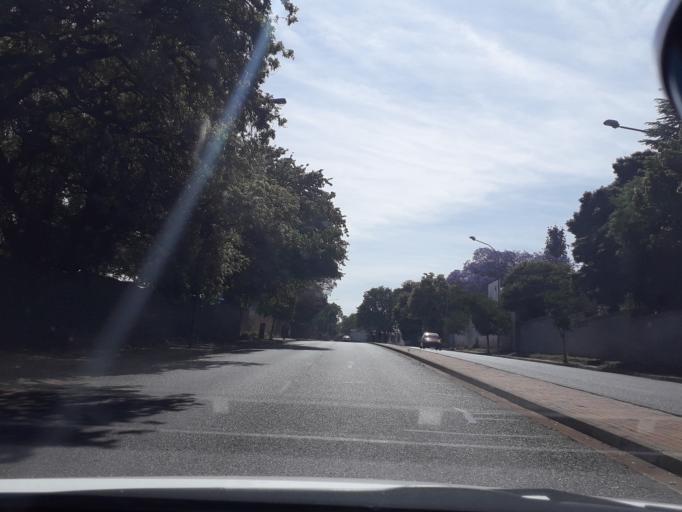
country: ZA
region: Gauteng
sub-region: City of Johannesburg Metropolitan Municipality
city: Johannesburg
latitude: -26.1785
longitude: 28.0549
